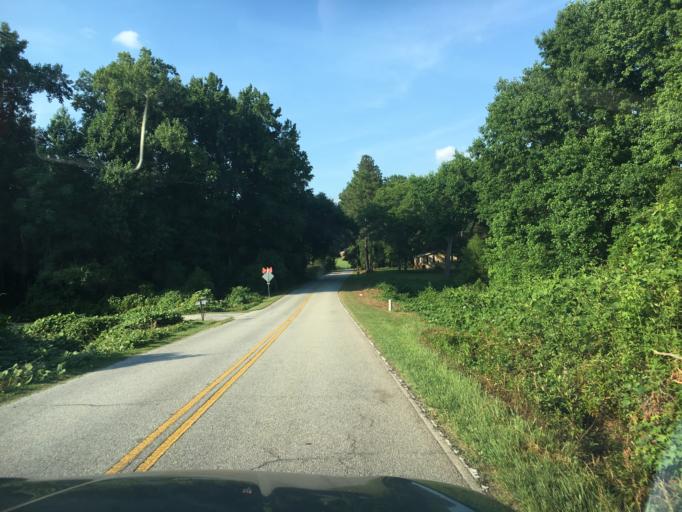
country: US
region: South Carolina
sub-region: Spartanburg County
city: Duncan
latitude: 34.8576
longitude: -82.1183
